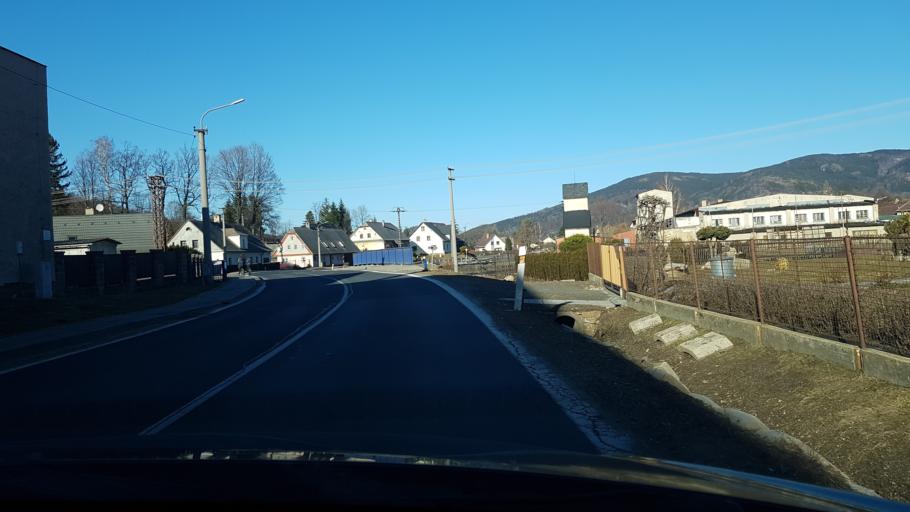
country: CZ
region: Olomoucky
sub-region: Okres Jesenik
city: Jesenik
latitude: 50.2001
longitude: 17.1948
